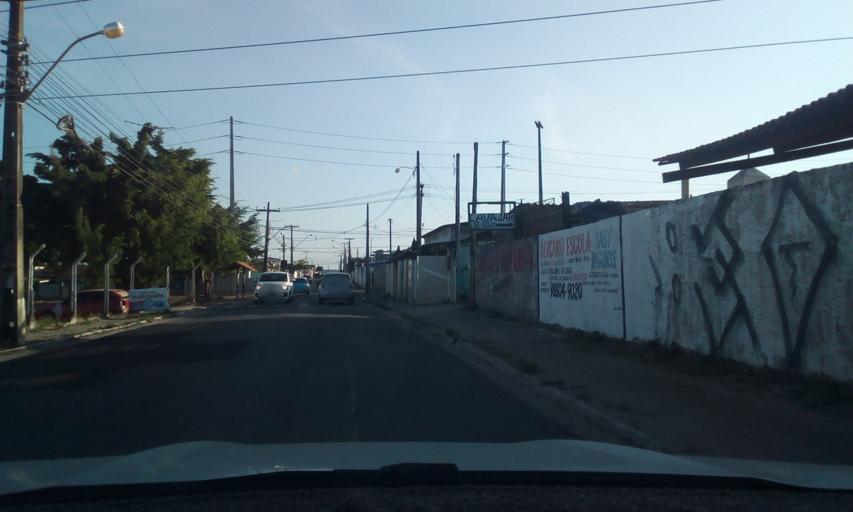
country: BR
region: Paraiba
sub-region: Bayeux
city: Bayeux
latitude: -7.1784
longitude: -34.8953
